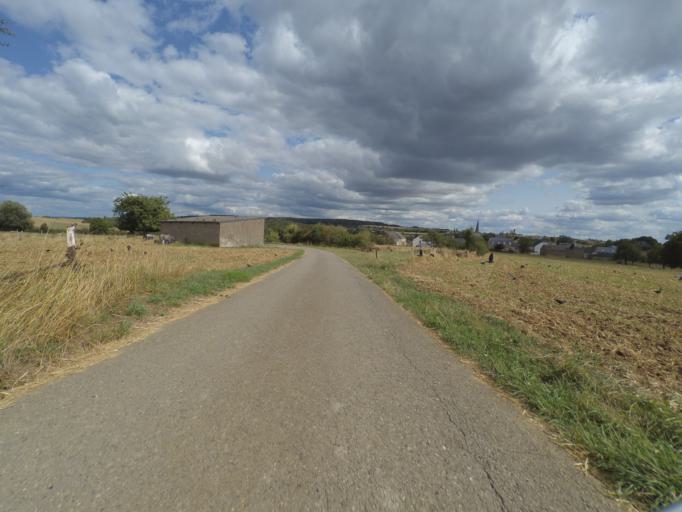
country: LU
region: Grevenmacher
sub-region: Canton de Remich
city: Mondorf-les-Bains
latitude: 49.5222
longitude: 6.2942
